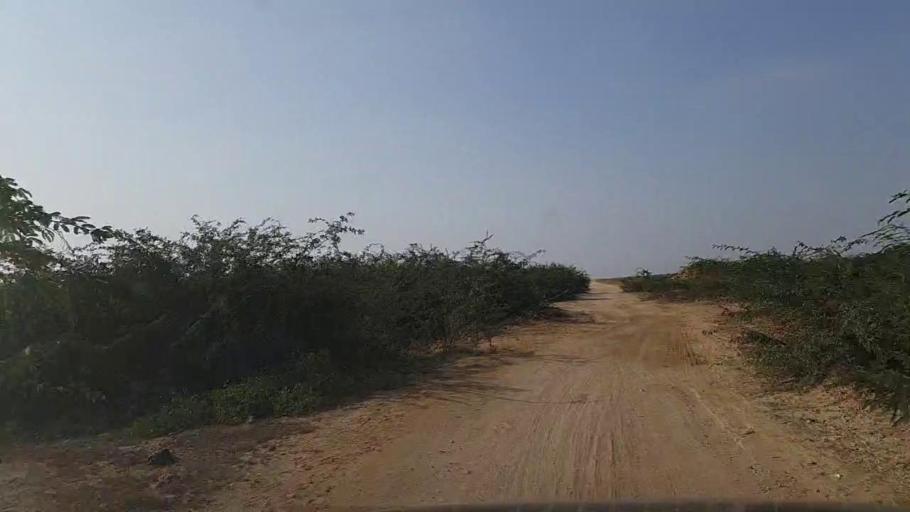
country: PK
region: Sindh
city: Gharo
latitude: 24.7494
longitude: 67.5574
